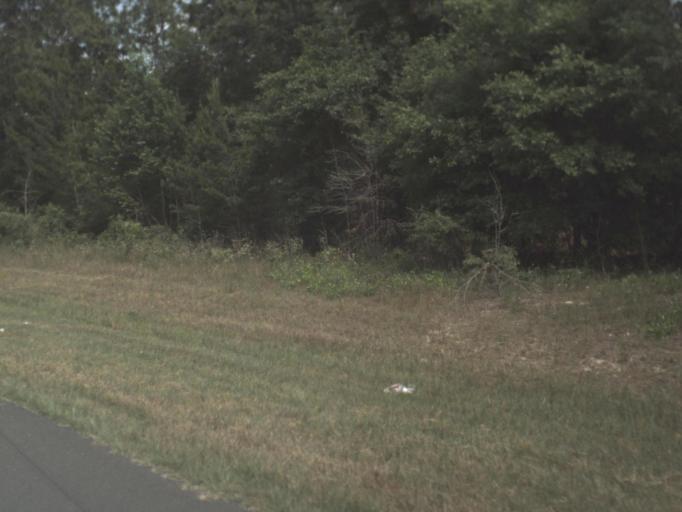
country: US
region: Florida
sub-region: Putnam County
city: Interlachen
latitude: 29.6256
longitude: -81.9047
